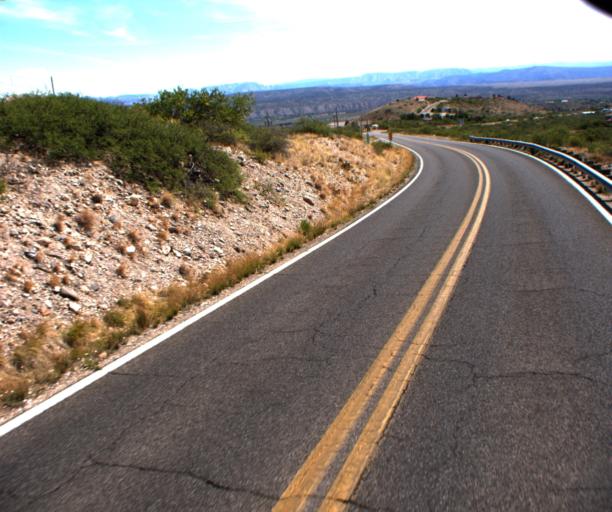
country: US
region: Arizona
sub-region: Yavapai County
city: Clarkdale
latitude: 34.7593
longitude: -112.0817
